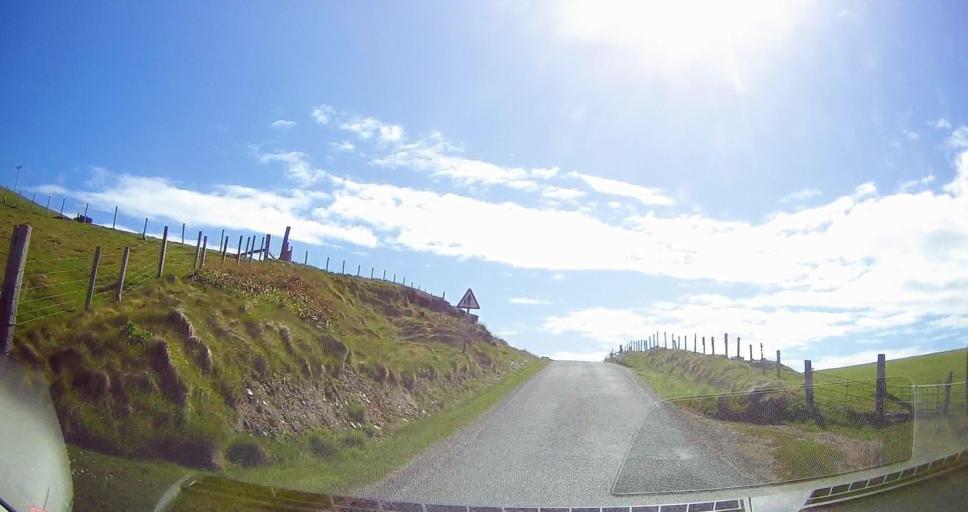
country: GB
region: Scotland
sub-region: Shetland Islands
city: Sandwick
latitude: 59.9619
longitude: -1.3232
